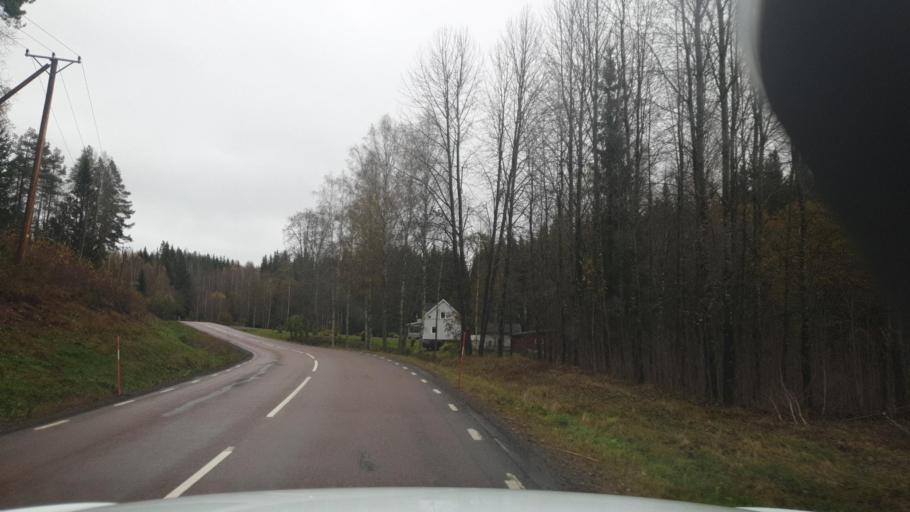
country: SE
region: Vaermland
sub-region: Eda Kommun
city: Charlottenberg
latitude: 59.8069
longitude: 12.2083
